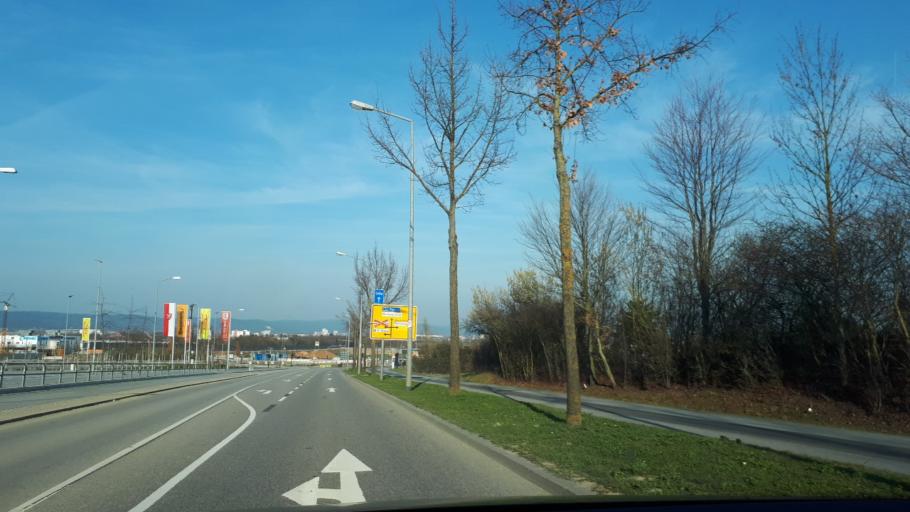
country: DE
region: Bavaria
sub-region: Upper Palatinate
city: Regensburg
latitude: 48.9901
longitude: 12.1091
